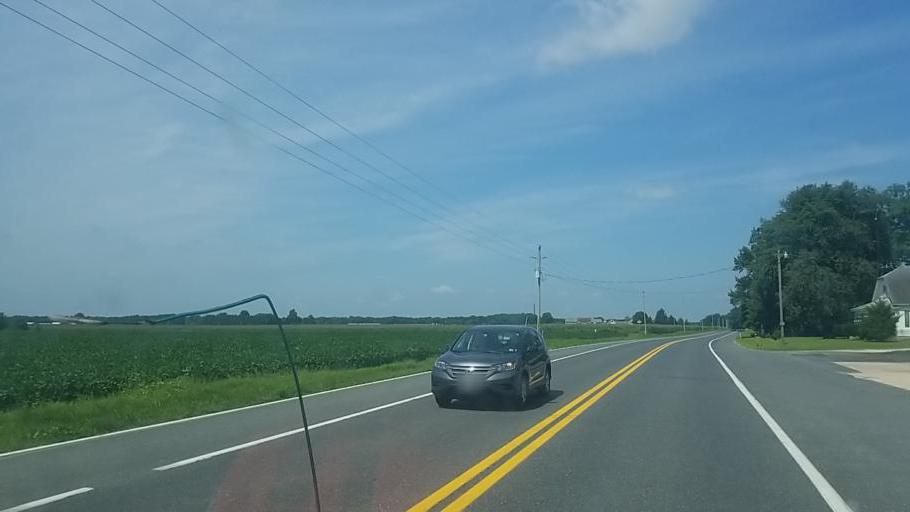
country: US
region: Delaware
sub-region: Sussex County
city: Bridgeville
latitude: 38.8262
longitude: -75.6529
